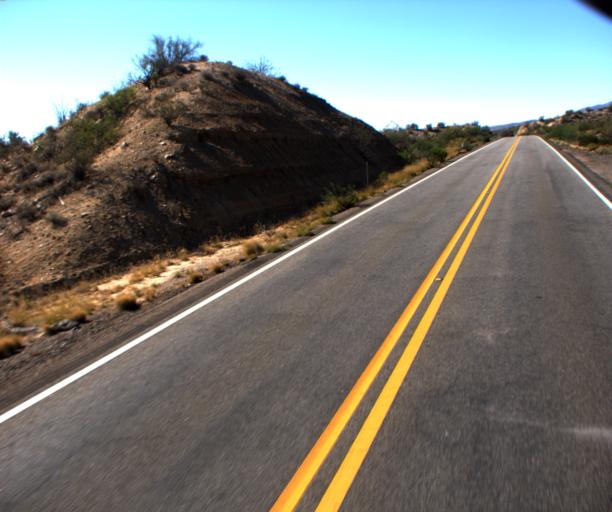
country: US
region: Arizona
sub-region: Yavapai County
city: Bagdad
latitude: 34.7802
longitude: -113.6227
